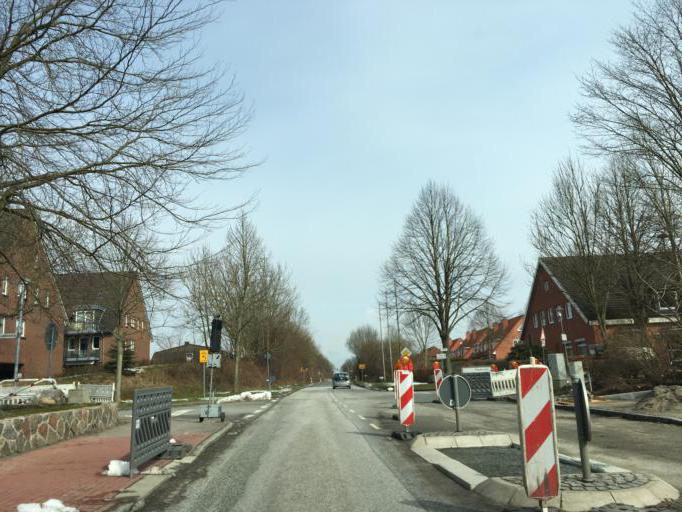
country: DE
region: Schleswig-Holstein
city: Escheburg
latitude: 53.4668
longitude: 10.3094
